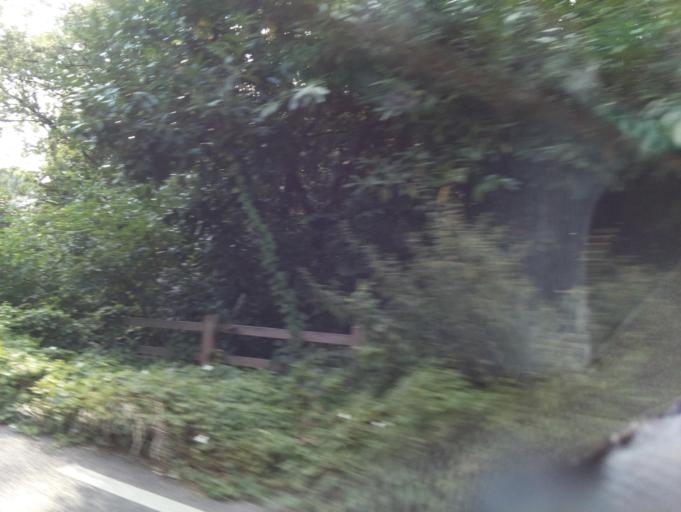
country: GB
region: England
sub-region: Devon
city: Tiverton
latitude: 50.8927
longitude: -3.4961
